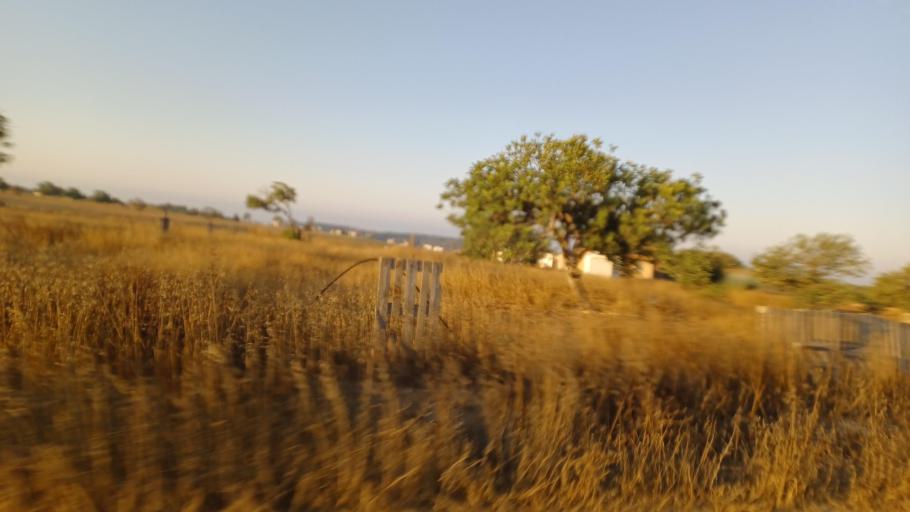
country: CY
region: Larnaka
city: Xylotymbou
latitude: 35.0007
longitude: 33.7777
